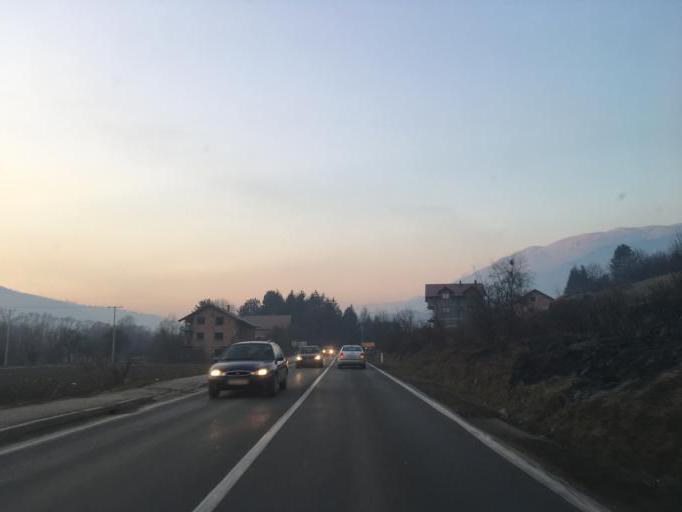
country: BA
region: Federation of Bosnia and Herzegovina
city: Travnik
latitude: 44.2152
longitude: 17.6980
